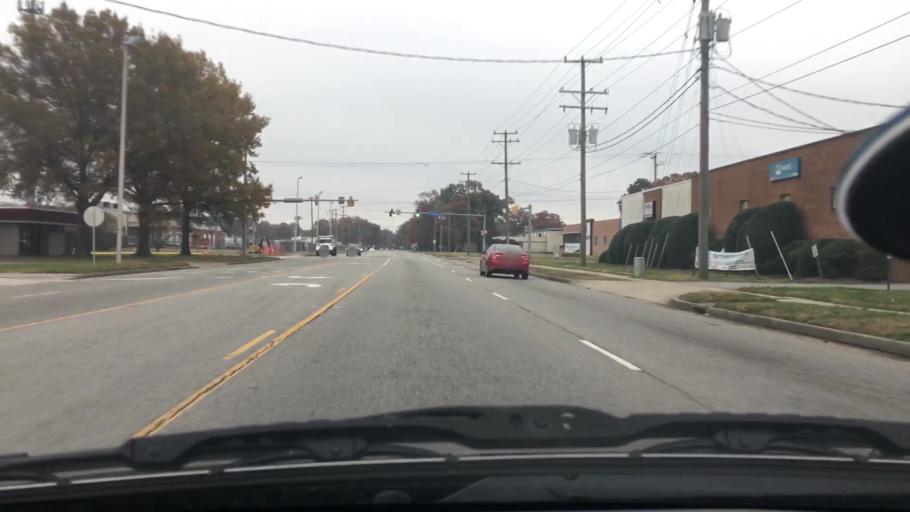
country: US
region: Virginia
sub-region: City of Norfolk
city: Norfolk
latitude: 36.8596
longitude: -76.2428
